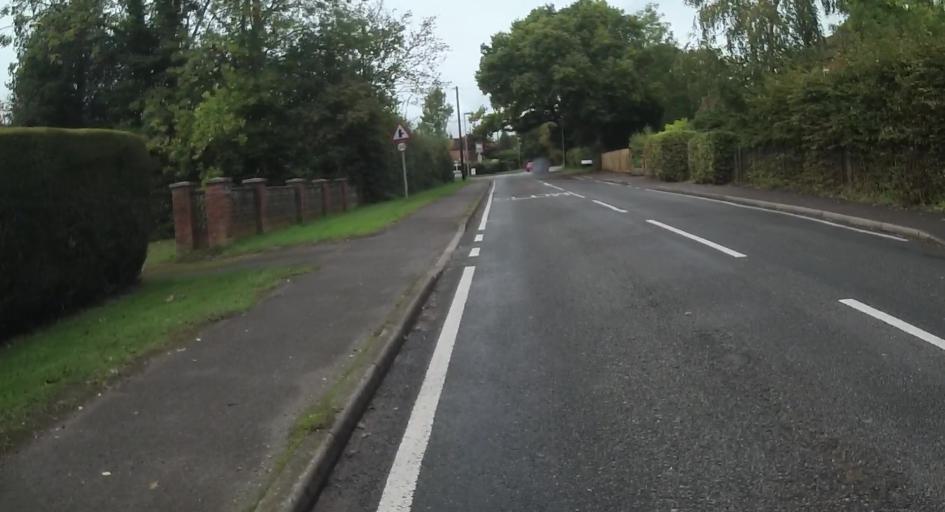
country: GB
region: England
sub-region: Hampshire
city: Tadley
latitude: 51.3520
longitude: -1.1680
